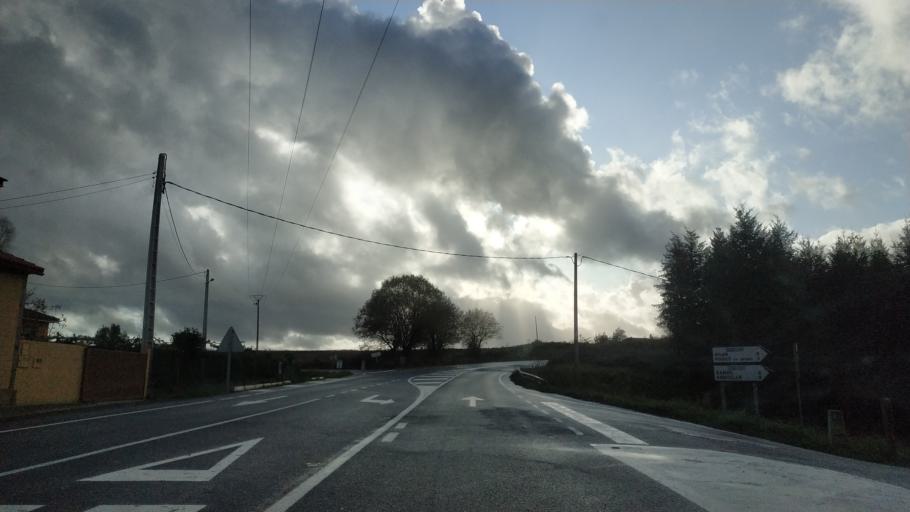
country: ES
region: Galicia
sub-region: Provincia da Coruna
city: Arzua
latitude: 42.9600
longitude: -8.1497
